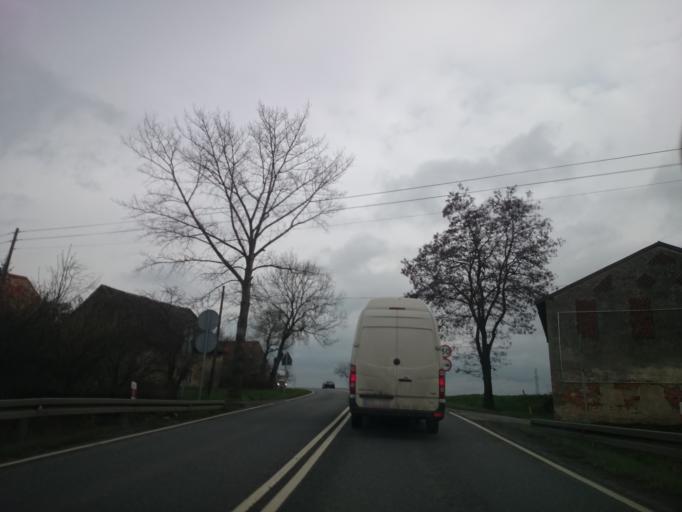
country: PL
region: Opole Voivodeship
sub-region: Powiat nyski
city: Paczkow
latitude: 50.4542
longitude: 17.0425
